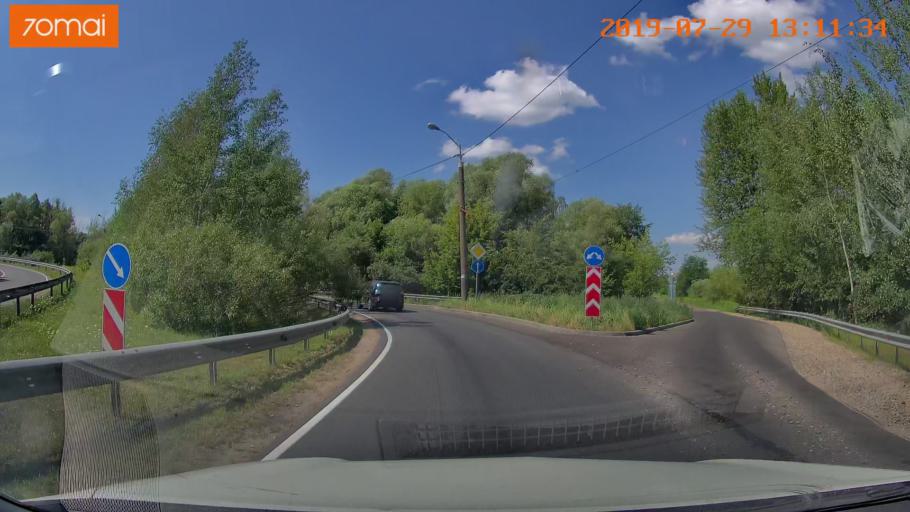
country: RU
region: Kaliningrad
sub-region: Gorod Kaliningrad
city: Kaliningrad
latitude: 54.7199
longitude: 20.3853
